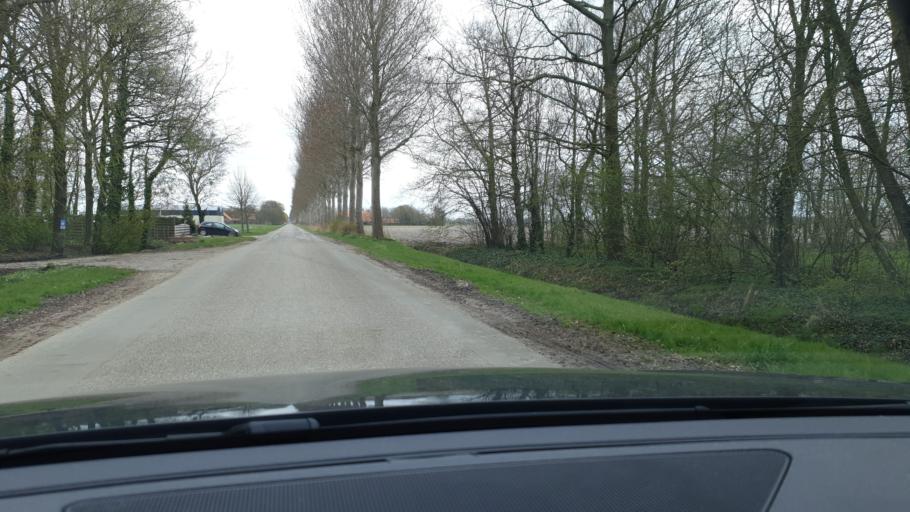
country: NL
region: Flevoland
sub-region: Gemeente Urk
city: Urk
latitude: 52.7393
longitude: 5.6137
